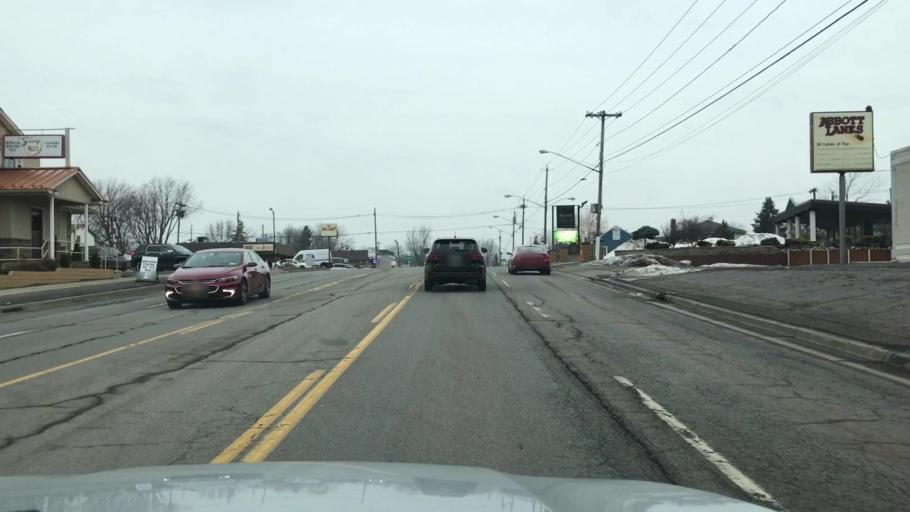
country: US
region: New York
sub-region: Erie County
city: Lackawanna
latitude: 42.8145
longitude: -78.8003
